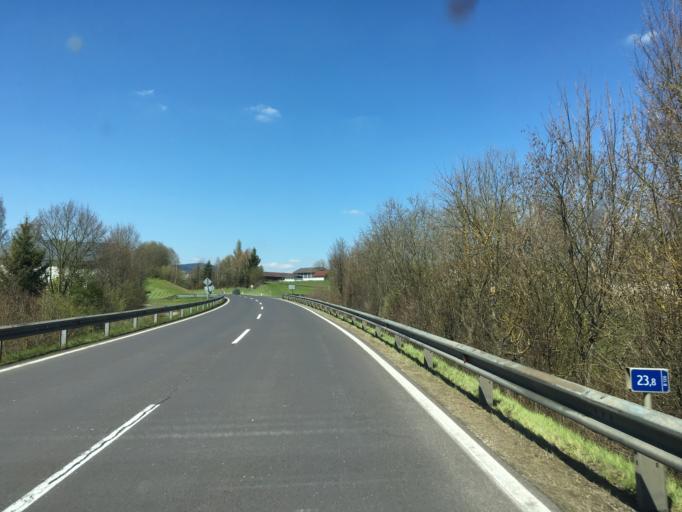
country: AT
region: Upper Austria
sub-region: Politischer Bezirk Urfahr-Umgebung
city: Bad Leonfelden
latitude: 48.4967
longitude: 14.3020
